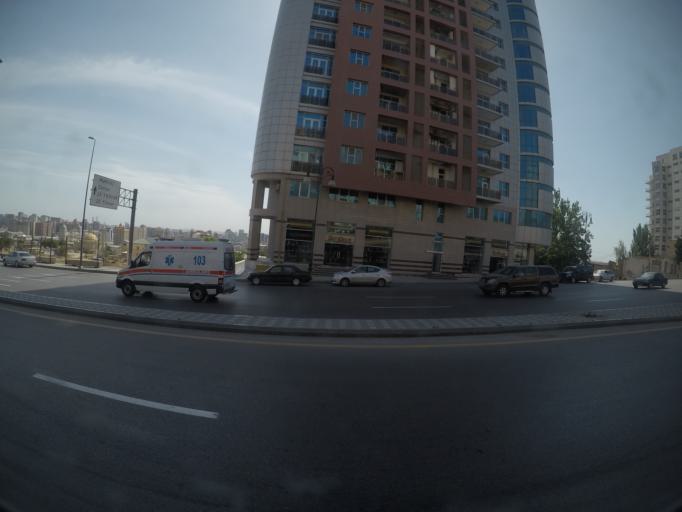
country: AZ
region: Baki
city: Badamdar
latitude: 40.3697
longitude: 49.8247
